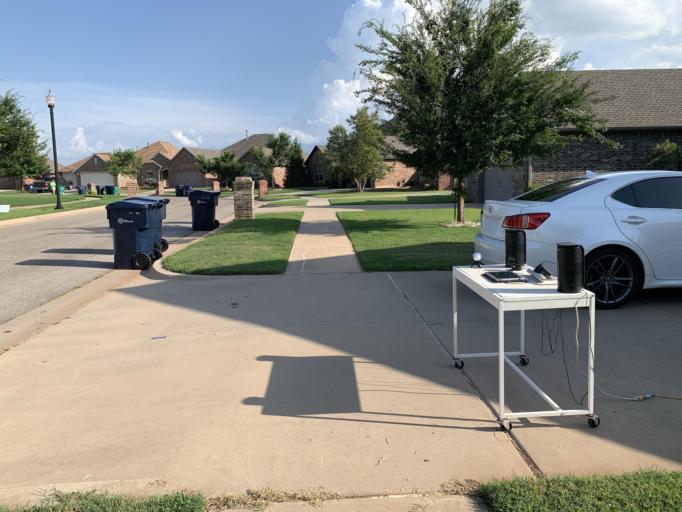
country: US
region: Oklahoma
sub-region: Oklahoma County
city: Edmond
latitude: 35.6641
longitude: -97.5709
